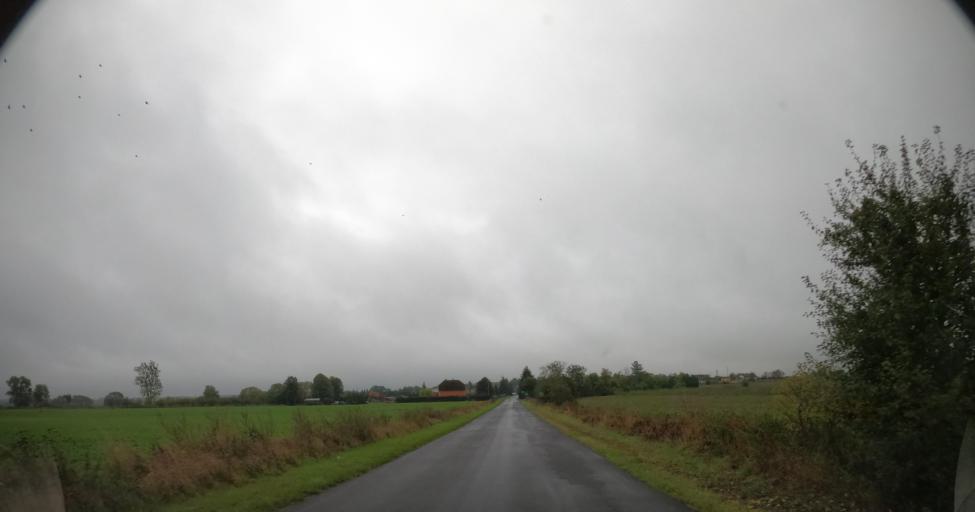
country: PL
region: West Pomeranian Voivodeship
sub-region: Powiat pyrzycki
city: Kozielice
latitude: 53.0524
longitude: 14.7761
